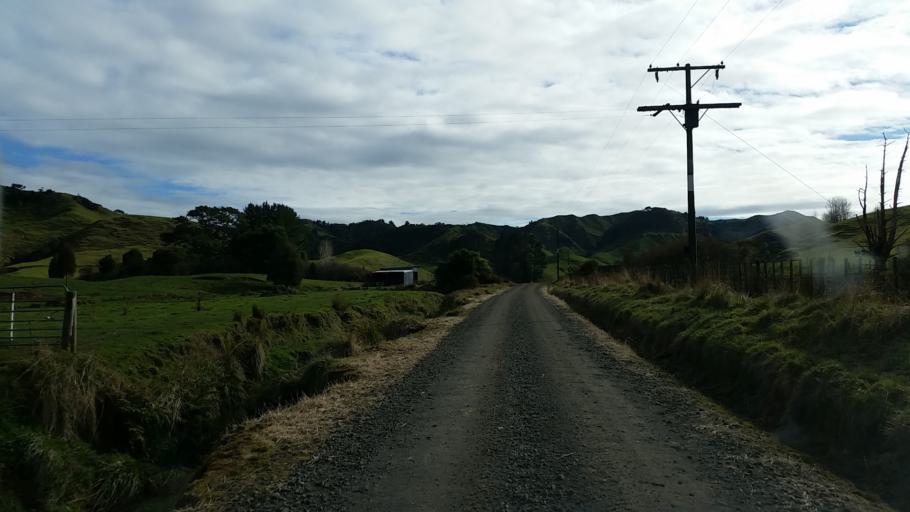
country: NZ
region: Taranaki
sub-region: South Taranaki District
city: Eltham
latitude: -39.2308
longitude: 174.5662
